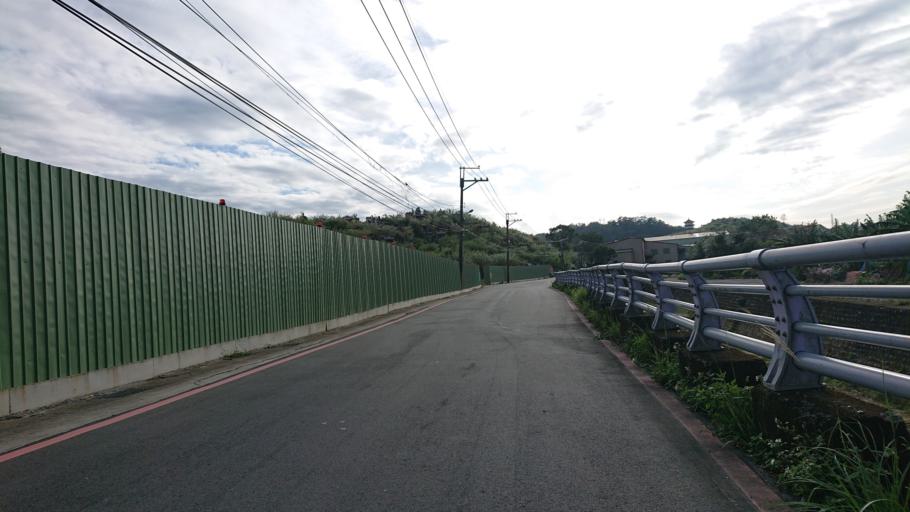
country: TW
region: Taiwan
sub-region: Taoyuan
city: Taoyuan
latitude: 24.9244
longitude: 121.3641
